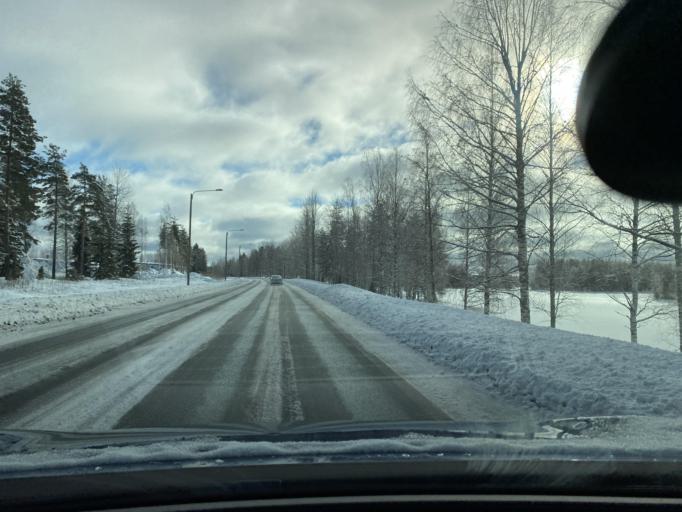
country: FI
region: Southern Savonia
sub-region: Mikkeli
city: Kangasniemi
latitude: 62.0084
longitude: 26.6403
